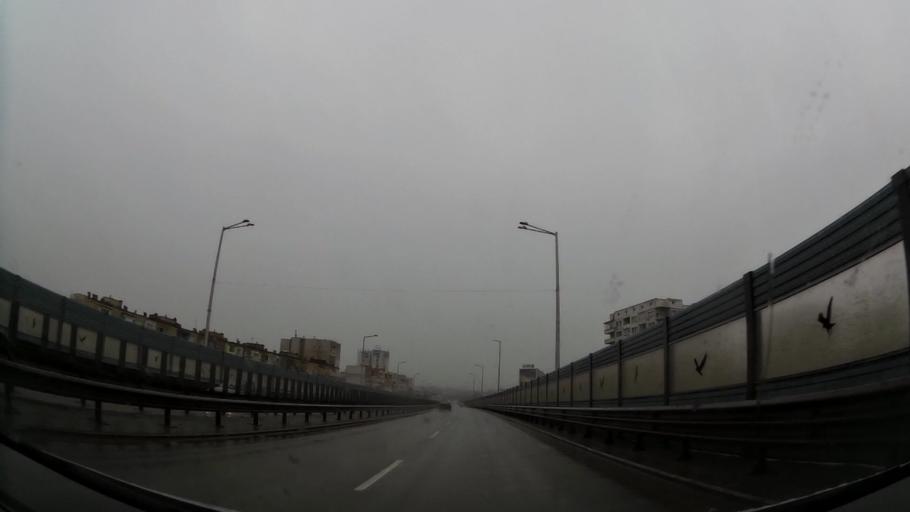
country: BG
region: Sofia-Capital
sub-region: Stolichna Obshtina
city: Sofia
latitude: 42.6690
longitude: 23.3928
